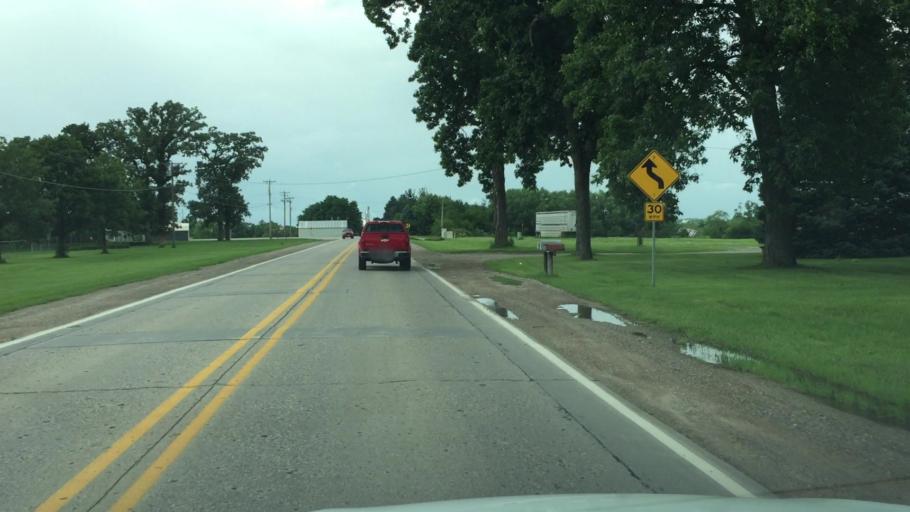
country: US
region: Iowa
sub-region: Jasper County
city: Newton
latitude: 41.7186
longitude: -93.0579
